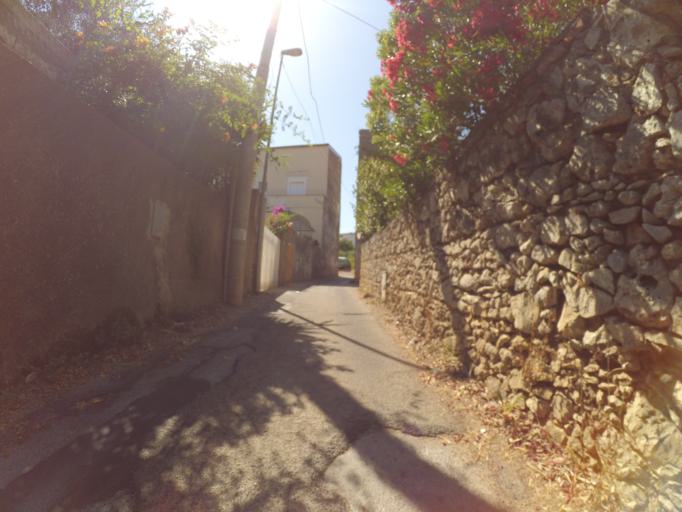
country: IT
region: Latium
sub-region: Provincia di Latina
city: Gaeta
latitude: 41.2185
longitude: 13.5517
